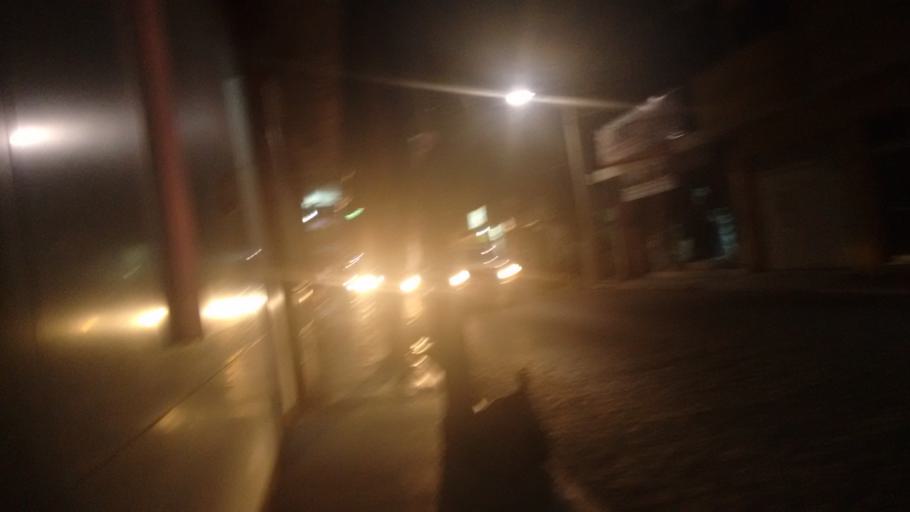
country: MX
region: Campeche
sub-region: Carmen
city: Ciudad del Carmen
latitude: 18.6384
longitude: -91.8340
